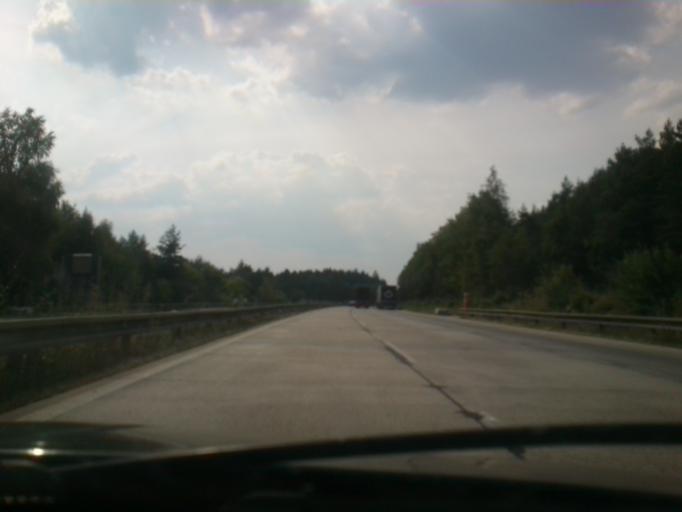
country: CZ
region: Central Bohemia
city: Trhovy Stepanov
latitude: 49.7495
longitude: 14.9949
